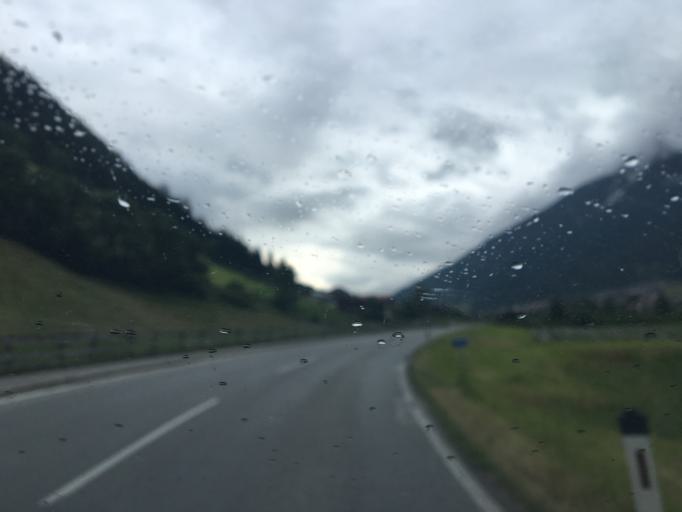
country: AT
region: Tyrol
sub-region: Politischer Bezirk Innsbruck Land
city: Neustift im Stubaital
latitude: 47.1172
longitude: 11.3157
